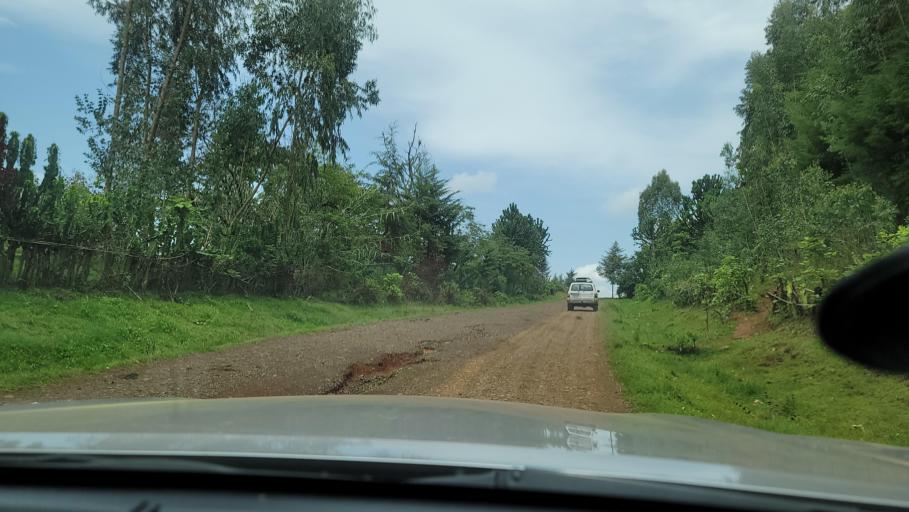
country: ET
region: Southern Nations, Nationalities, and People's Region
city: Bonga
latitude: 7.7015
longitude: 36.2510
